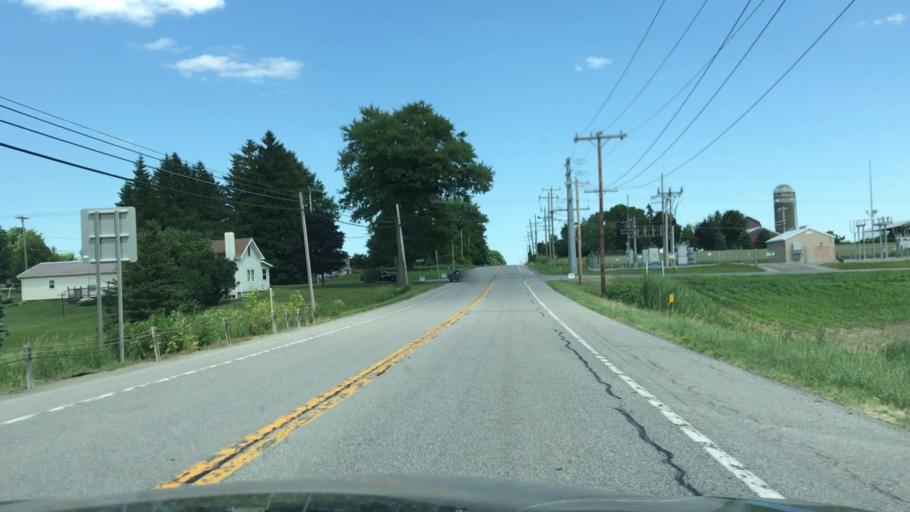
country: US
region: New York
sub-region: Wyoming County
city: Perry
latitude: 42.7471
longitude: -78.0265
